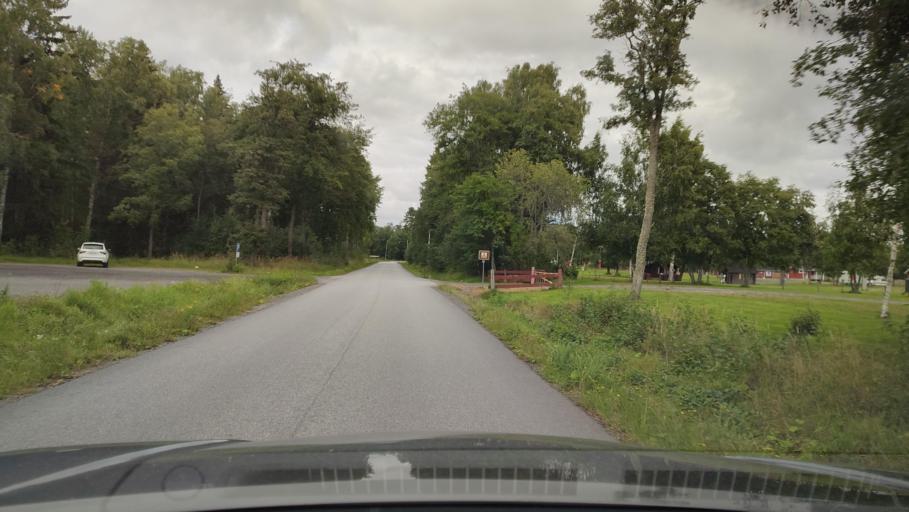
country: FI
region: Ostrobothnia
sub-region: Sydosterbotten
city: Kristinestad
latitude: 62.2617
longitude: 21.3604
